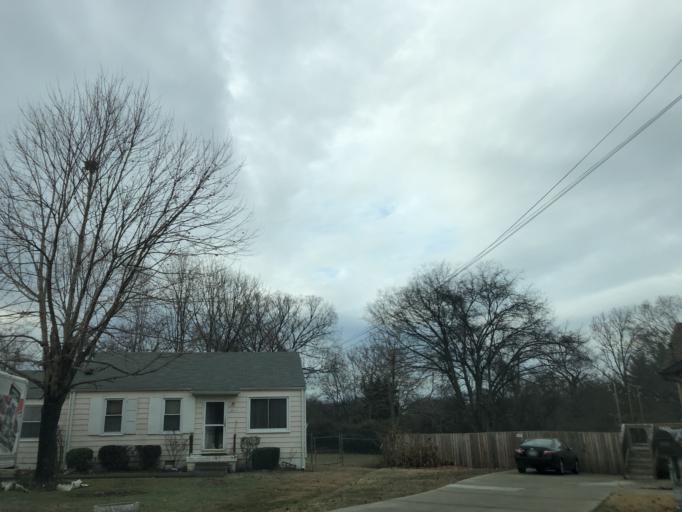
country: US
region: Tennessee
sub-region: Davidson County
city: Nashville
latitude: 36.2029
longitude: -86.7284
